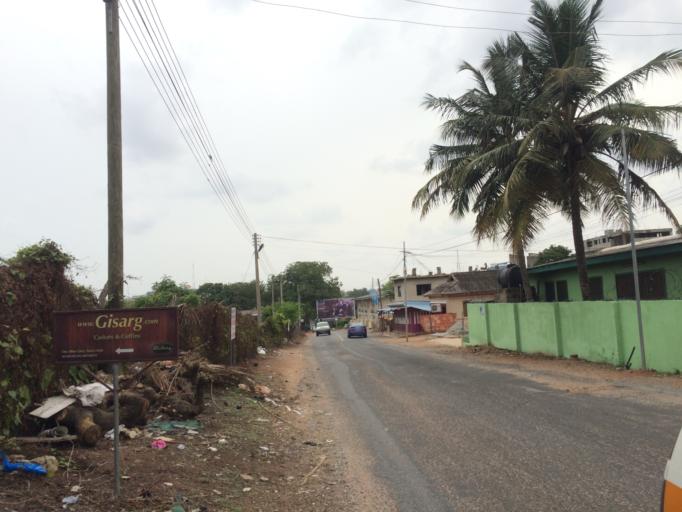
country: GH
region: Greater Accra
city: Accra
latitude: 5.5603
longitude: -0.1860
